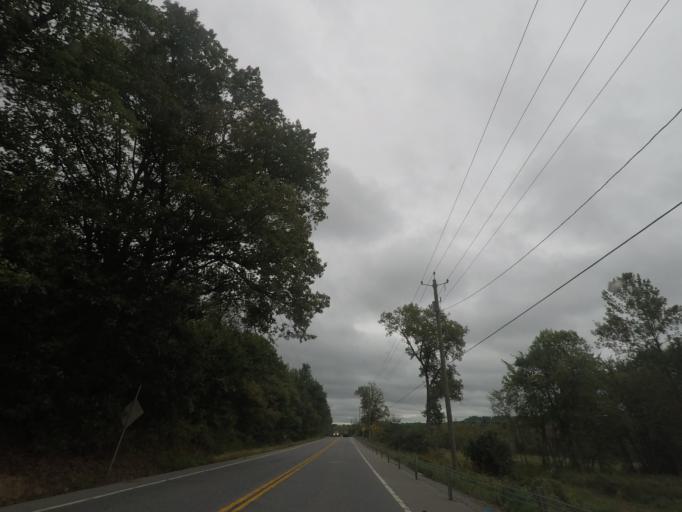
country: US
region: New York
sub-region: Saratoga County
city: Country Knolls
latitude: 42.9261
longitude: -73.7588
